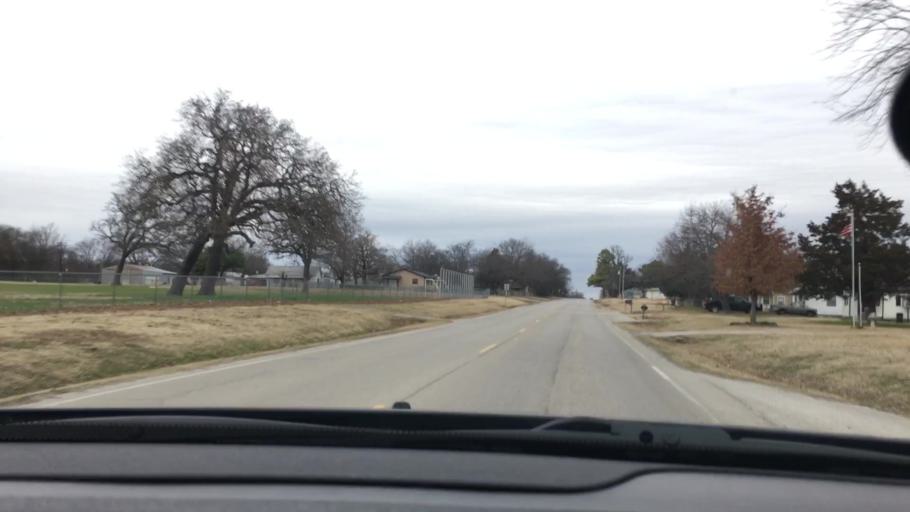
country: US
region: Oklahoma
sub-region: Carter County
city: Ardmore
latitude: 34.1714
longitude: -97.1081
